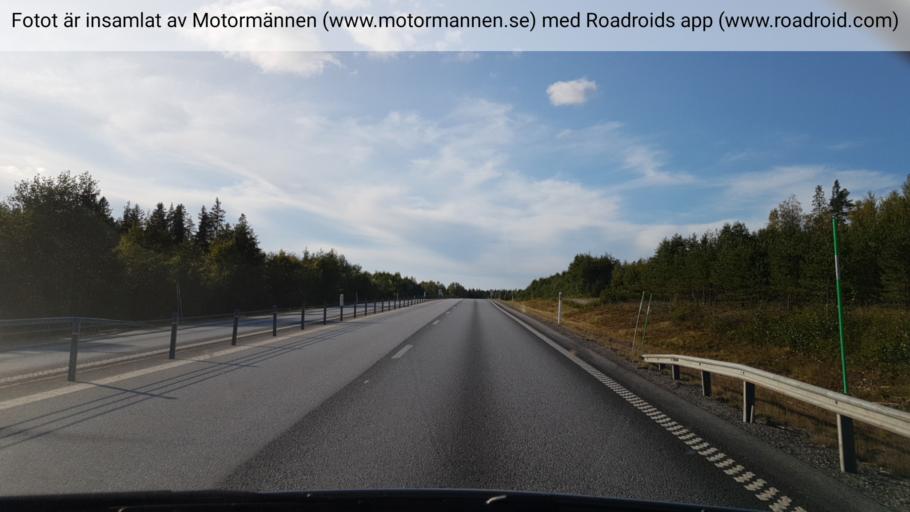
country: SE
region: Vaesterbotten
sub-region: Vannas Kommun
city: Vannasby
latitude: 63.8991
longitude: 19.9098
